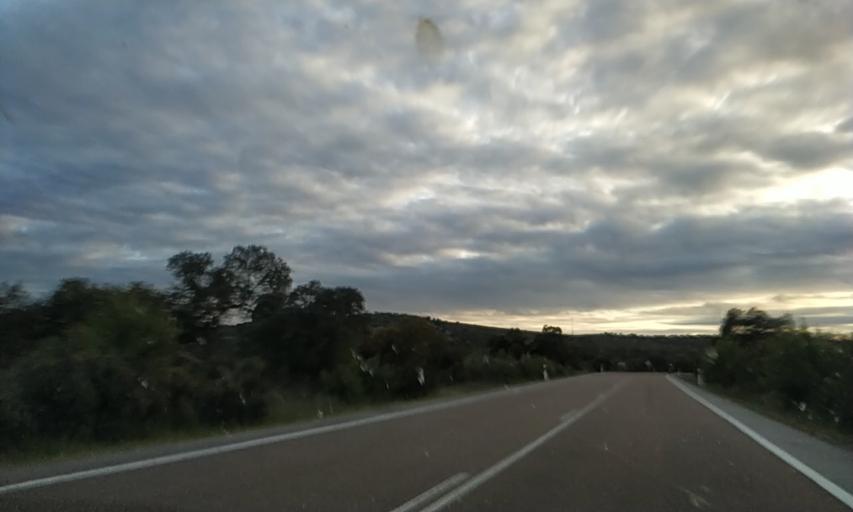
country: ES
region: Extremadura
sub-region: Provincia de Badajoz
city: Puebla de Obando
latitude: 39.2679
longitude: -6.5283
